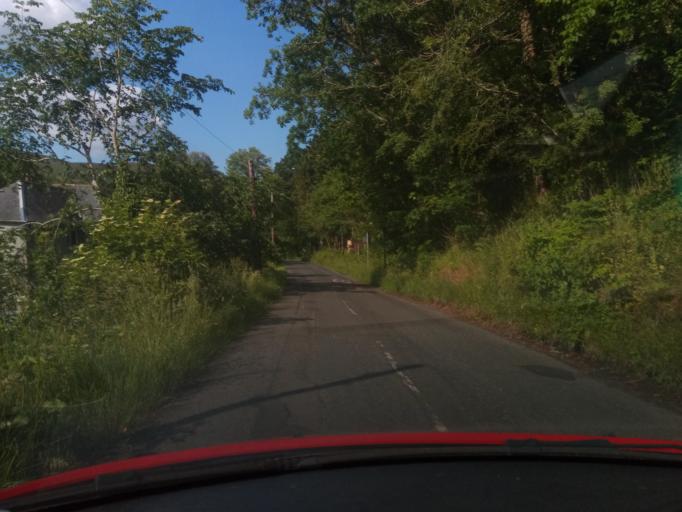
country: GB
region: Scotland
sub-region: The Scottish Borders
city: Selkirk
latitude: 55.5085
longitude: -2.9665
